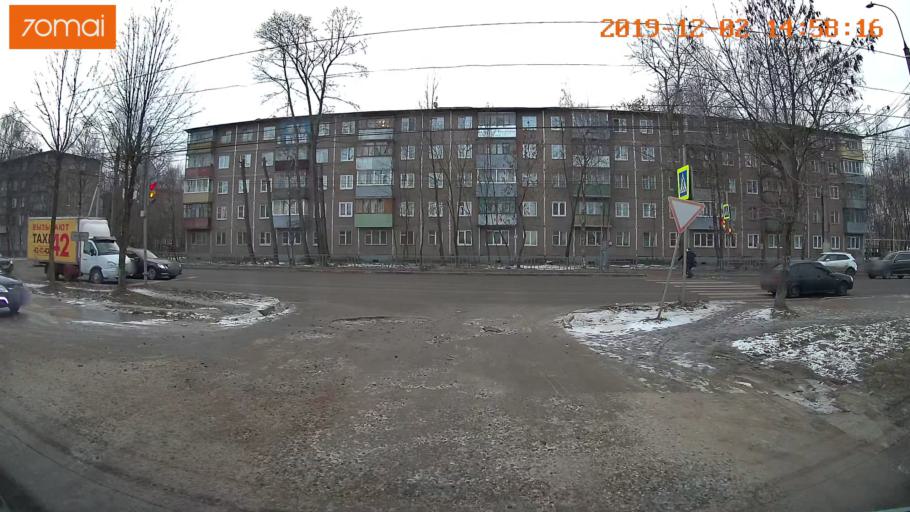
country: RU
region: Ivanovo
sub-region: Gorod Ivanovo
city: Ivanovo
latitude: 56.9736
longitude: 41.0102
